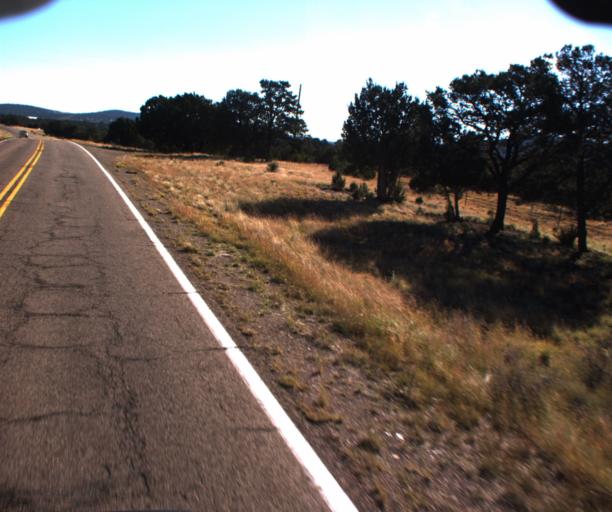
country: US
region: Arizona
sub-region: Navajo County
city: White Mountain Lake
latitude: 34.2911
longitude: -109.8085
